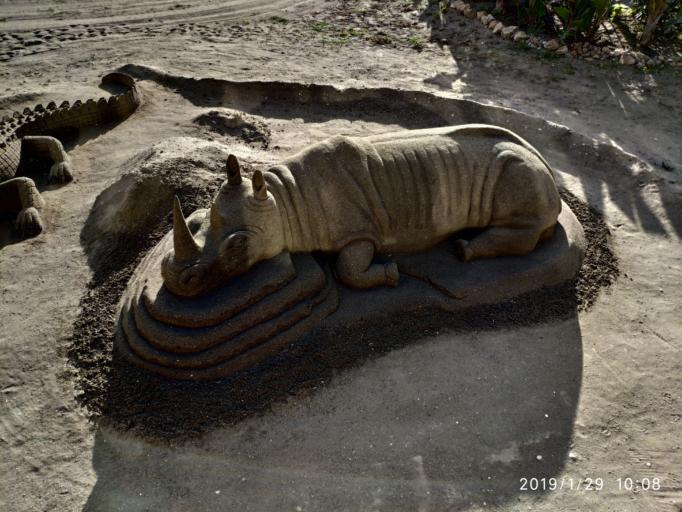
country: ES
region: Andalusia
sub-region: Provincia de Malaga
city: Torremolinos
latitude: 36.6070
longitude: -4.5057
